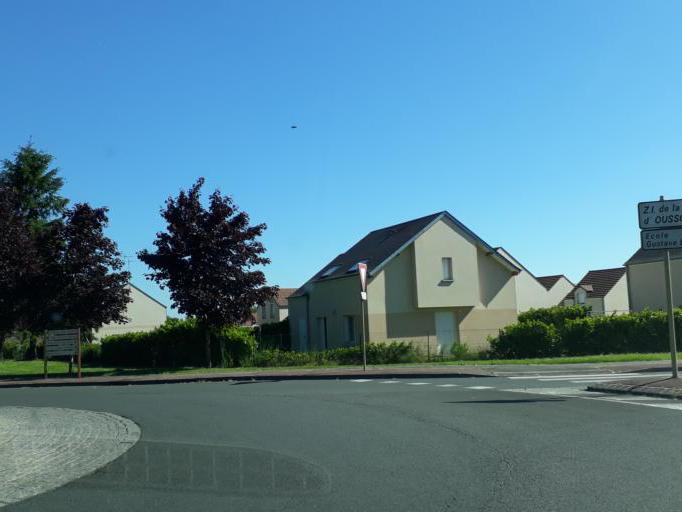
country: FR
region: Centre
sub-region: Departement du Loiret
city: Briare
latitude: 47.6311
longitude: 2.7475
